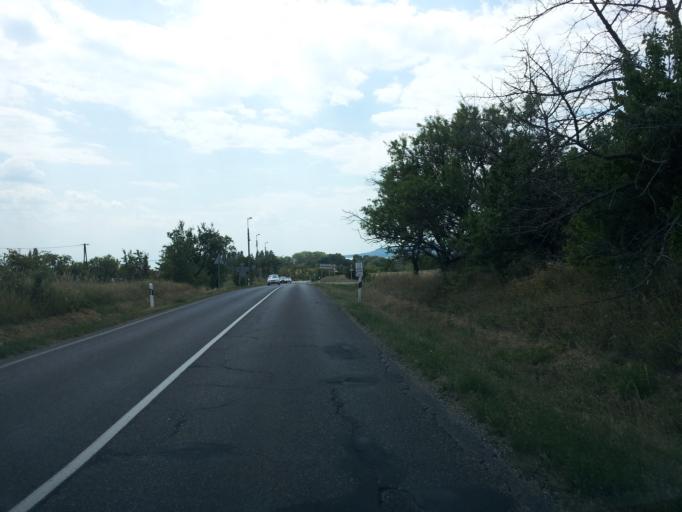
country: HU
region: Veszprem
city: Zanka
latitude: 46.8844
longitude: 17.7542
